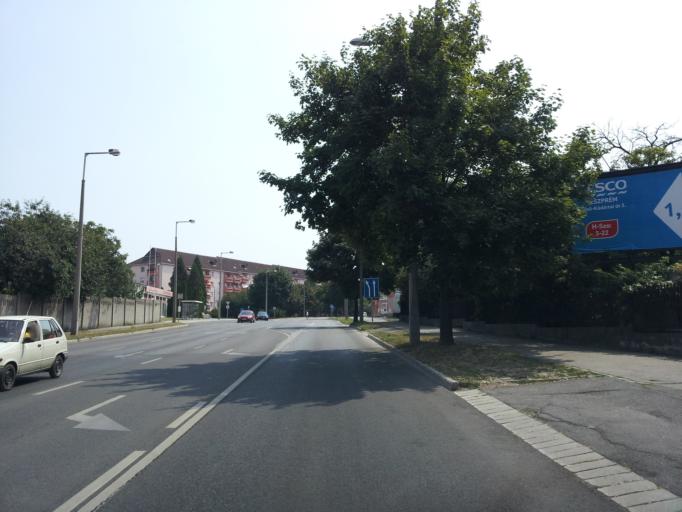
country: HU
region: Veszprem
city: Veszprem
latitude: 47.0981
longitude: 17.9262
